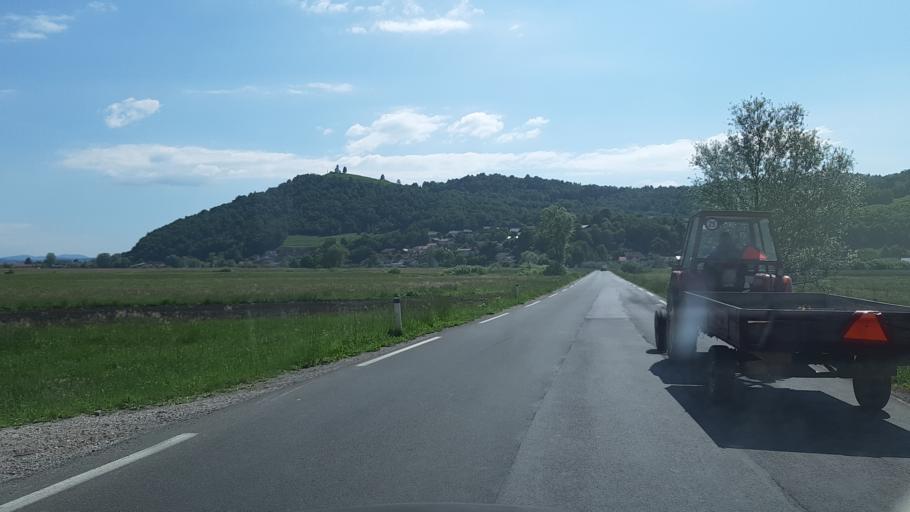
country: SI
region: Brezovica
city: Notranje Gorice
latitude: 45.9663
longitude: 14.4035
